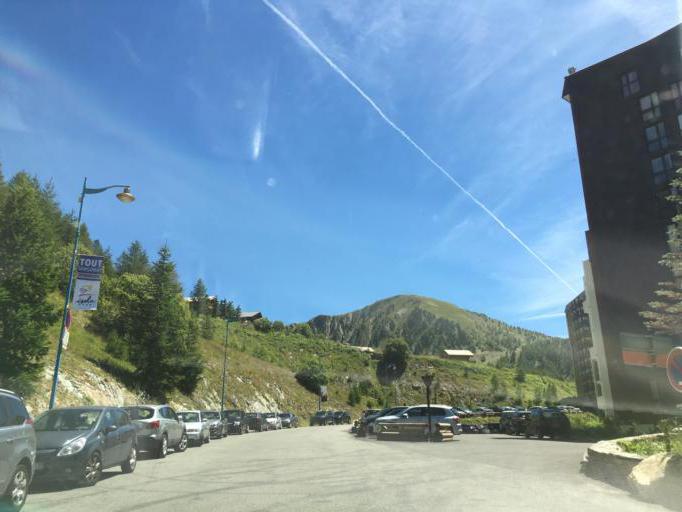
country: IT
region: Piedmont
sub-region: Provincia di Cuneo
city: Vinadio
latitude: 44.1847
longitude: 7.1613
